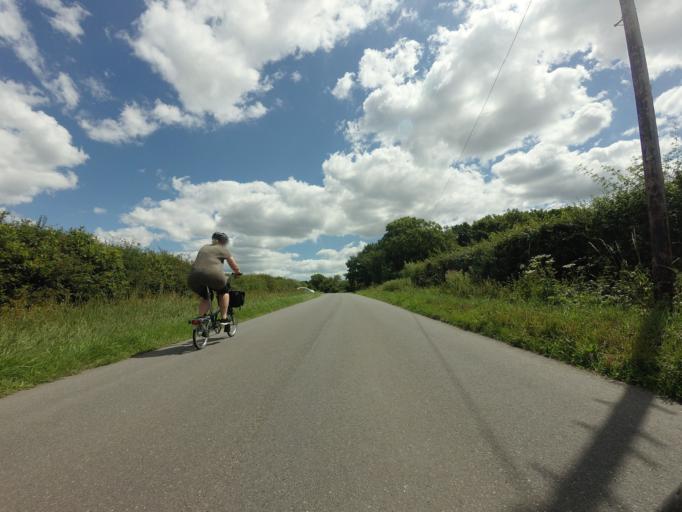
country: GB
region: England
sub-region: East Sussex
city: Hailsham
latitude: 50.8417
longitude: 0.1998
